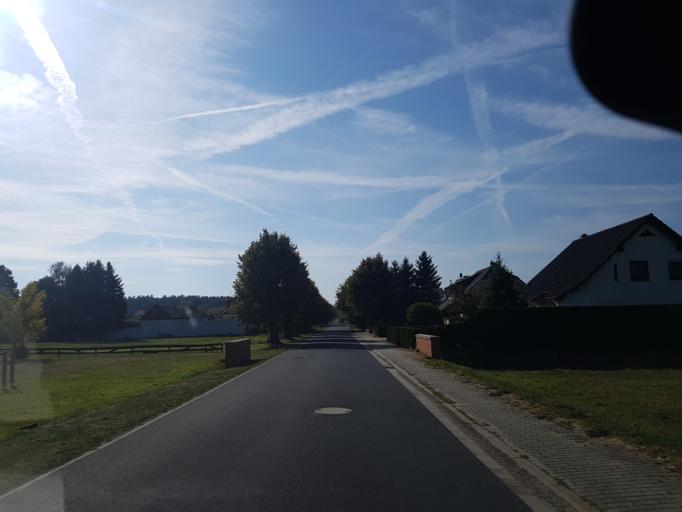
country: DE
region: Brandenburg
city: Hohenbucko
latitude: 51.7642
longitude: 13.4692
